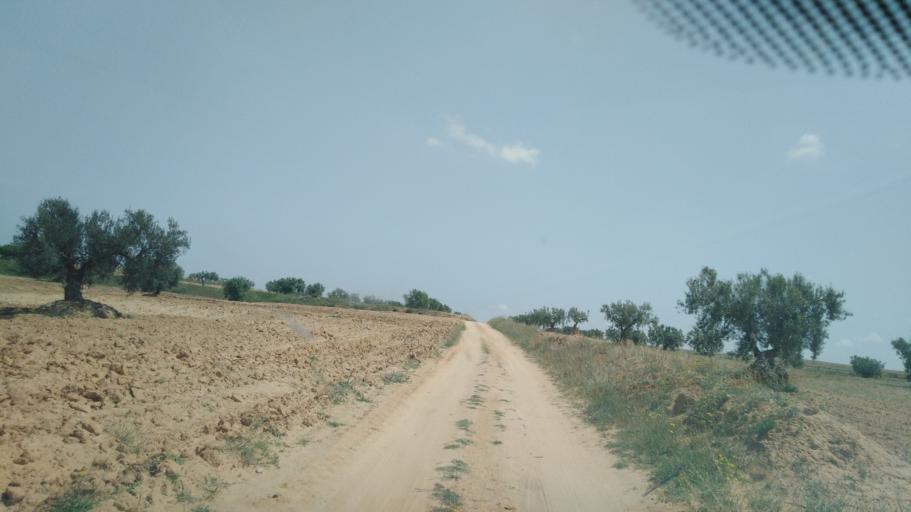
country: TN
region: Safaqis
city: Sfax
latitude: 34.7697
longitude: 10.5722
